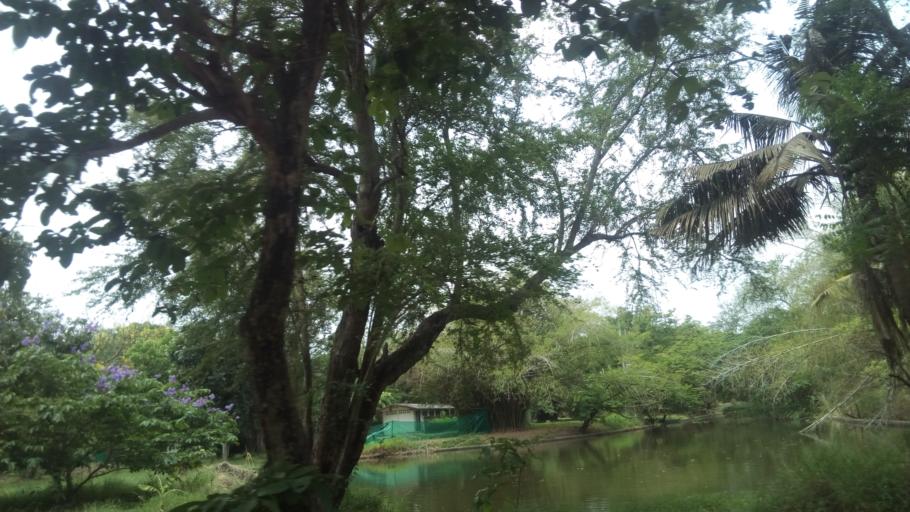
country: TH
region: Nakhon Pathom
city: Salaya
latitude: 13.7835
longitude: 100.3131
